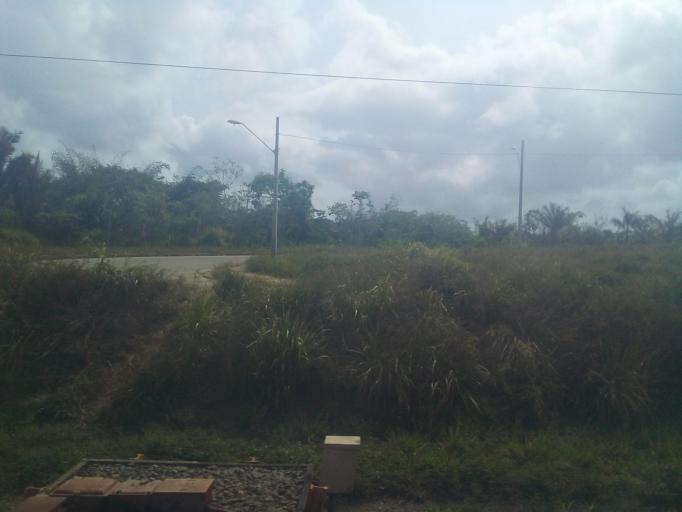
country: BR
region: Maranhao
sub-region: Itapecuru Mirim
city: Itapecuru Mirim
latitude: -3.0564
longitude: -44.3420
